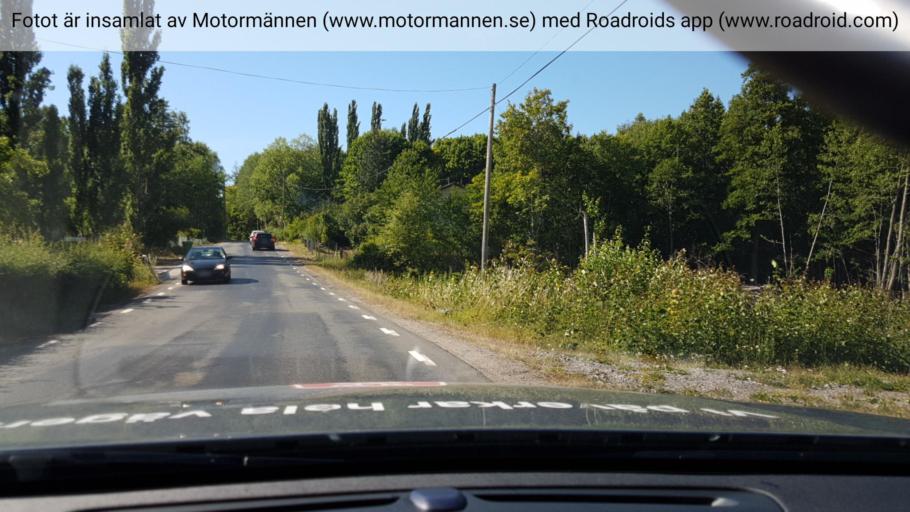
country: SE
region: Vaestra Goetaland
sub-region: Karlsborgs Kommun
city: Molltorp
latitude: 58.6694
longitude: 14.3706
